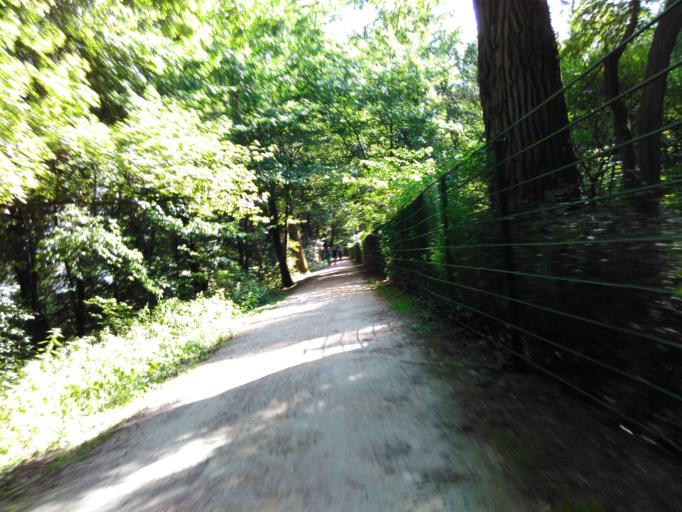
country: DE
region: Rheinland-Pfalz
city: Koblenz
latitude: 50.3296
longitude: 7.5893
